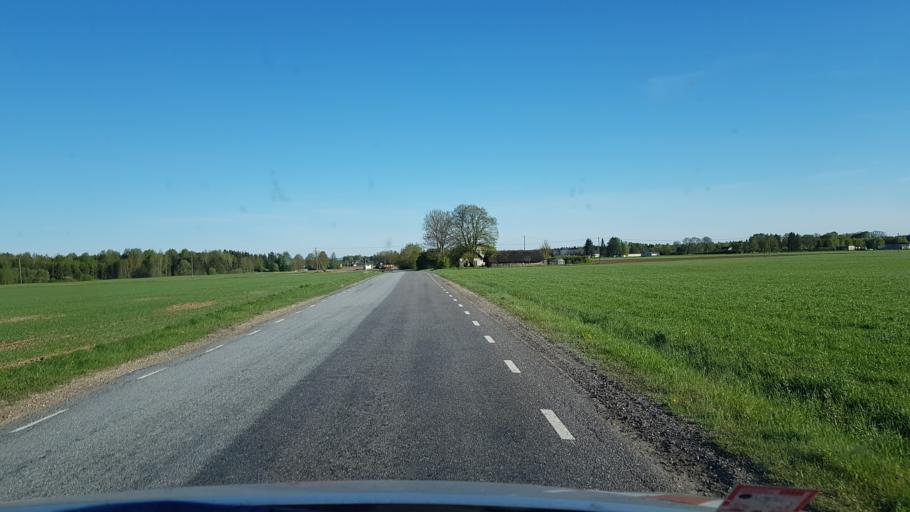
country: EE
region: Vorumaa
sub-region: Voru linn
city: Voru
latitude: 57.9210
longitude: 26.9513
